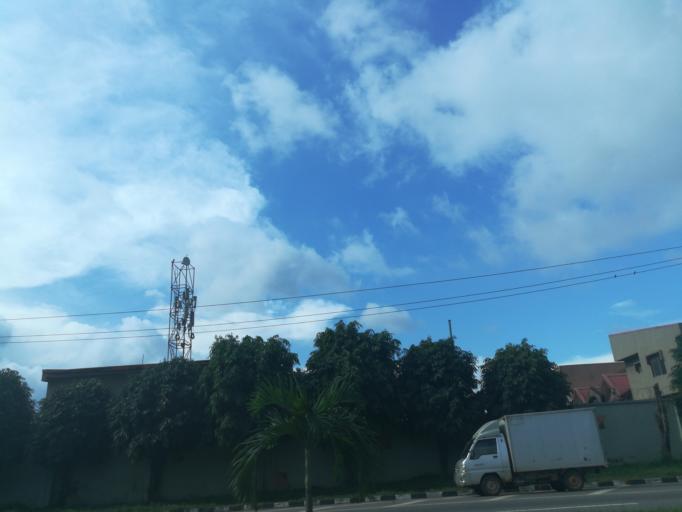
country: NG
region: Lagos
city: Ikeja
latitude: 6.6208
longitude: 3.3584
